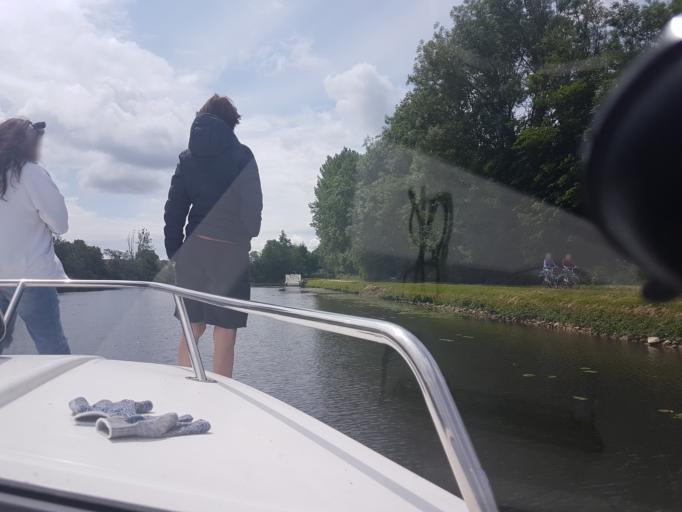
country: FR
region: Bourgogne
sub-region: Departement de l'Yonne
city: Augy
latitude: 47.7765
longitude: 3.6104
